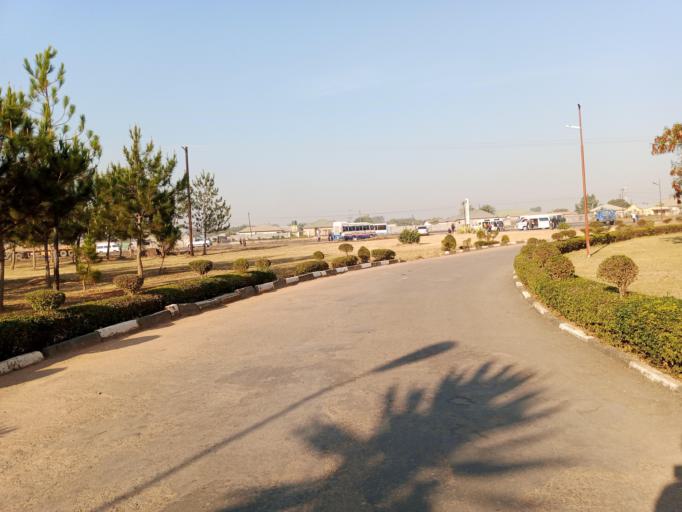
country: ZM
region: Copperbelt
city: Kitwe
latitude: -12.8753
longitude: 28.2531
